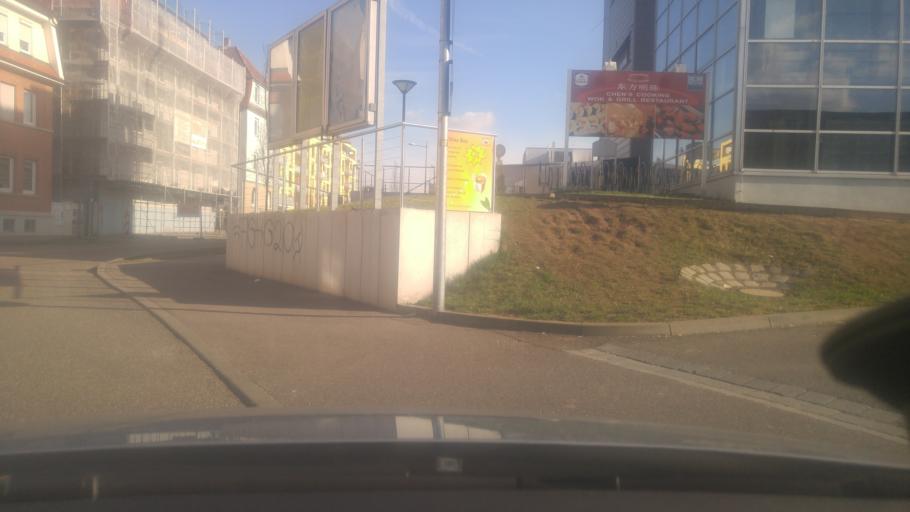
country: DE
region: Baden-Wuerttemberg
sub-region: Regierungsbezirk Stuttgart
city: Stuttgart Feuerbach
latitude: 48.8358
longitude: 9.1632
